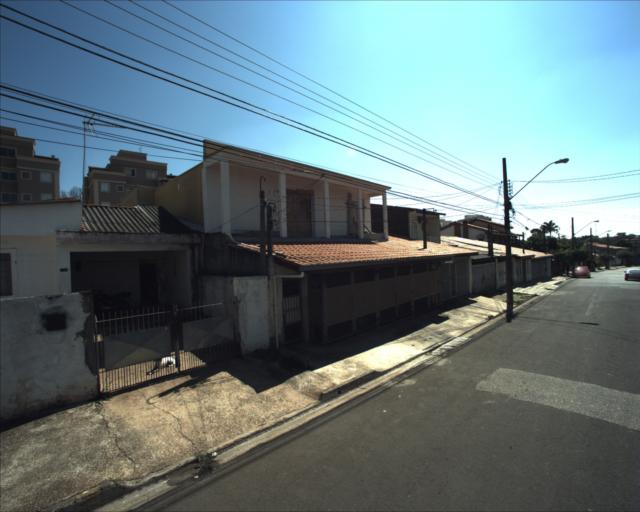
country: BR
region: Sao Paulo
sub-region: Sorocaba
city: Sorocaba
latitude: -23.4785
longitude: -47.4822
